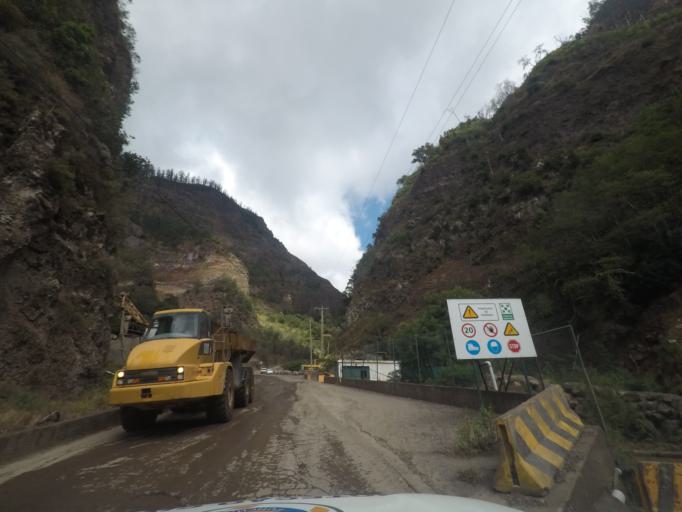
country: PT
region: Madeira
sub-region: Funchal
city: Nossa Senhora do Monte
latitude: 32.6877
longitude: -16.9157
